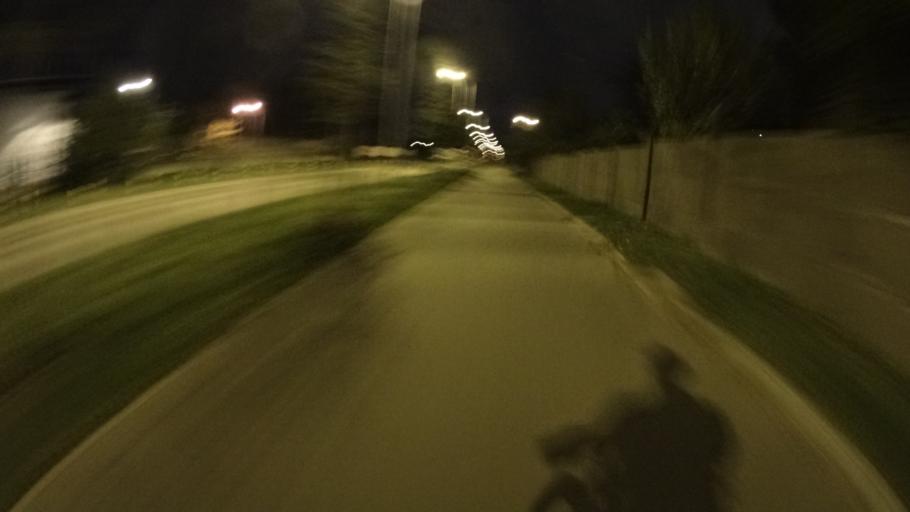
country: PL
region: Masovian Voivodeship
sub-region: Powiat pruszkowski
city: Otrebusy
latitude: 52.1632
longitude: 20.7670
